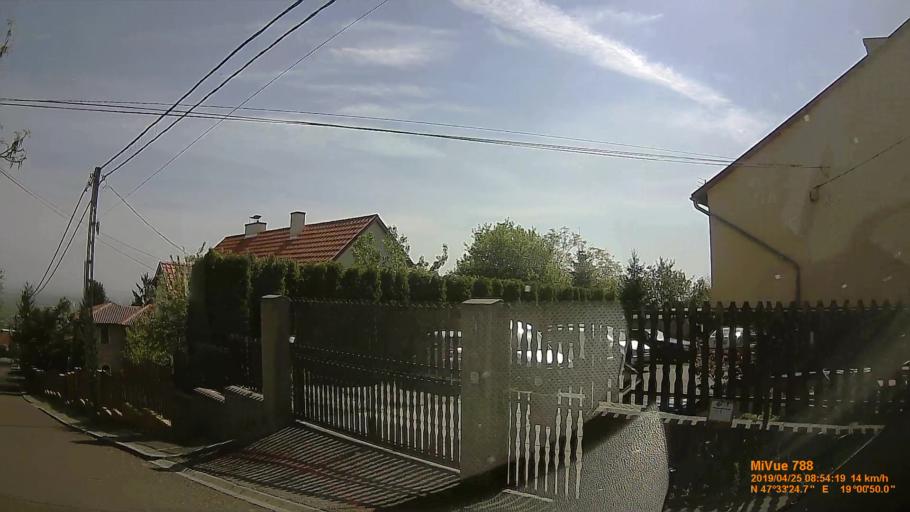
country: HU
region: Budapest
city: Budapest III. keruelet
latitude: 47.5569
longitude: 19.0139
